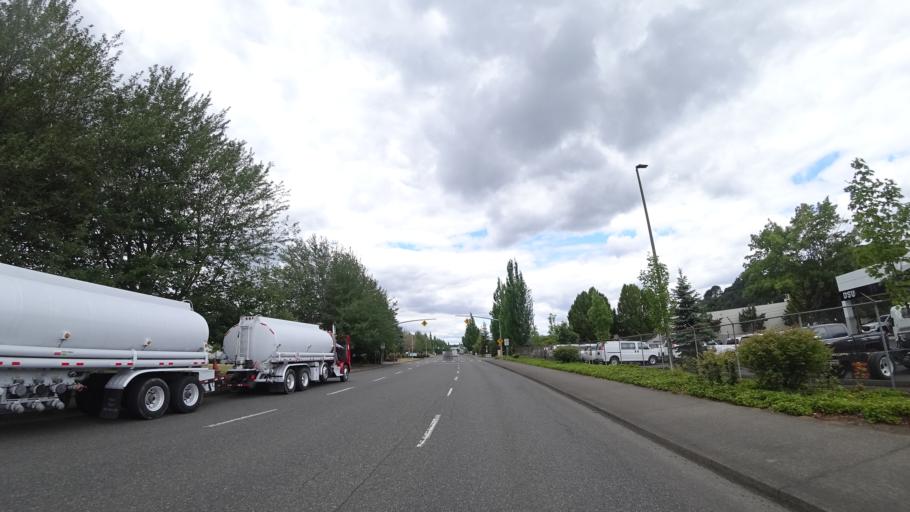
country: US
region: Oregon
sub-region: Multnomah County
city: Portland
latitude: 45.5573
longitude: -122.6987
